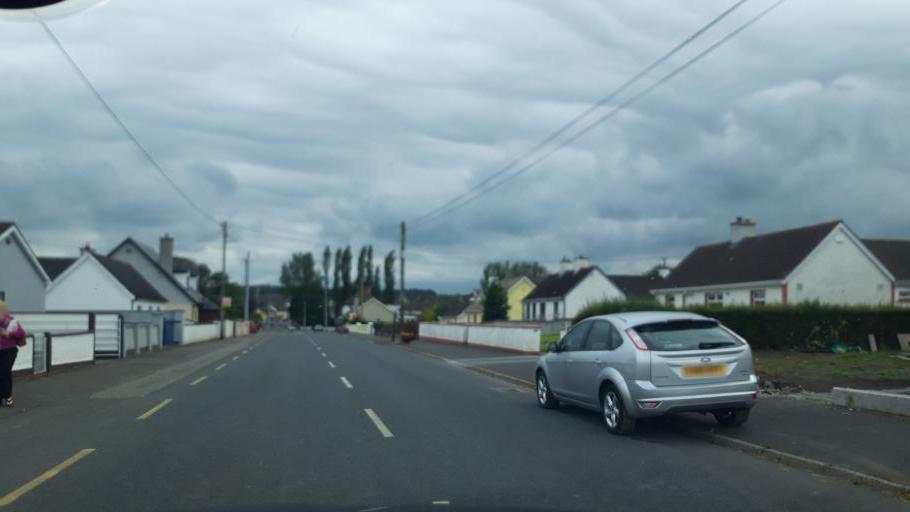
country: IE
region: Leinster
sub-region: Kilkenny
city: Ballyragget
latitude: 52.7356
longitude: -7.3986
